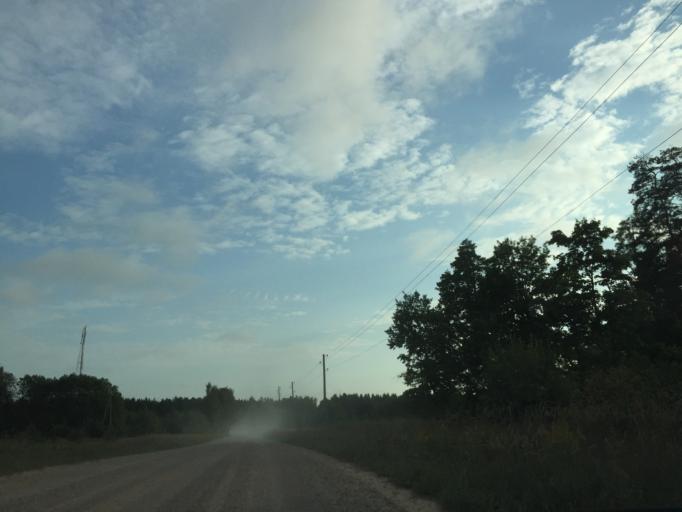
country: LV
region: Ikskile
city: Ikskile
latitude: 56.8152
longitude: 24.4483
